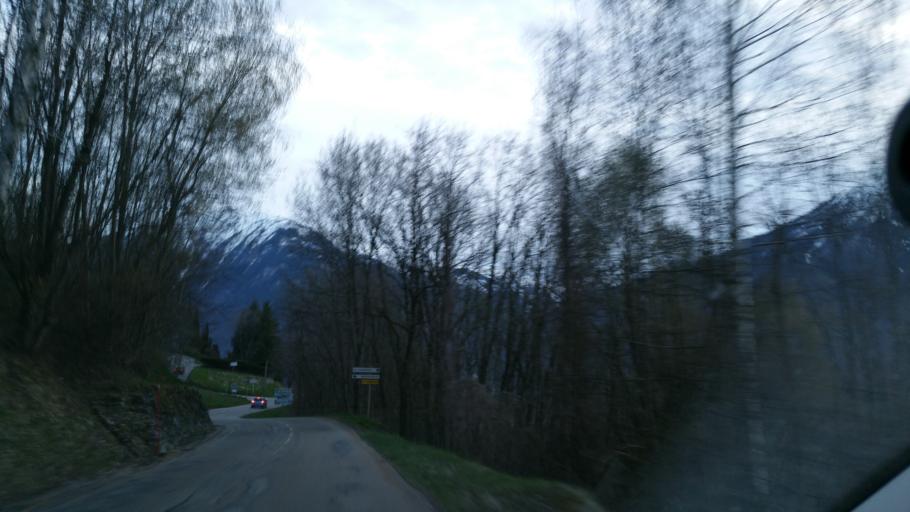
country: FR
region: Rhone-Alpes
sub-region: Departement de la Savoie
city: La Chambre
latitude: 45.3767
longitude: 6.3241
